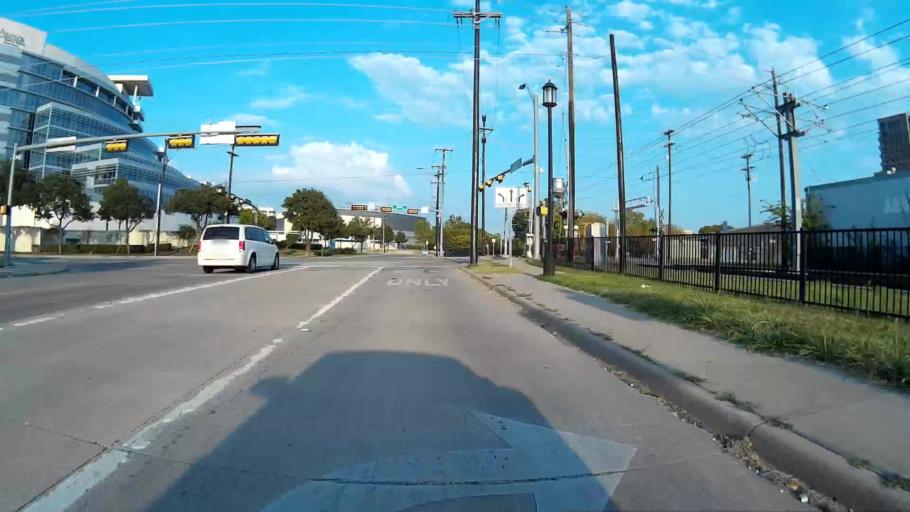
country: US
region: Texas
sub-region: Dallas County
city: Dallas
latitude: 32.7870
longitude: -96.7799
